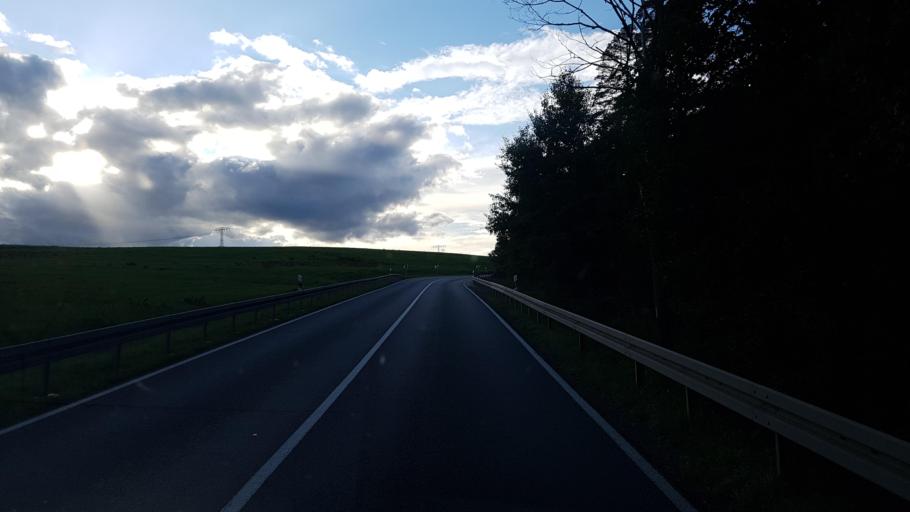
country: DE
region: Thuringia
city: Bad Lobenstein
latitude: 50.4486
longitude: 11.6677
